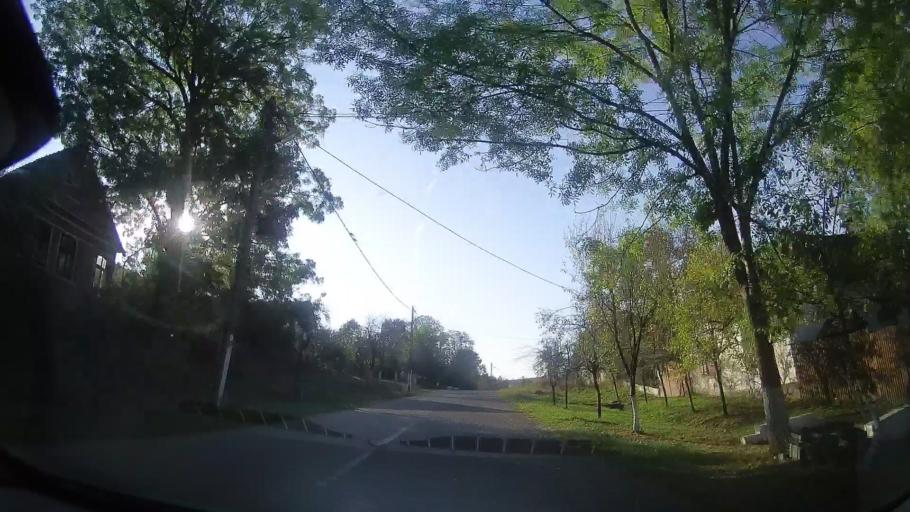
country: RO
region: Timis
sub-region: Comuna Bogda
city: Bogda
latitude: 45.9619
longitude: 21.6137
